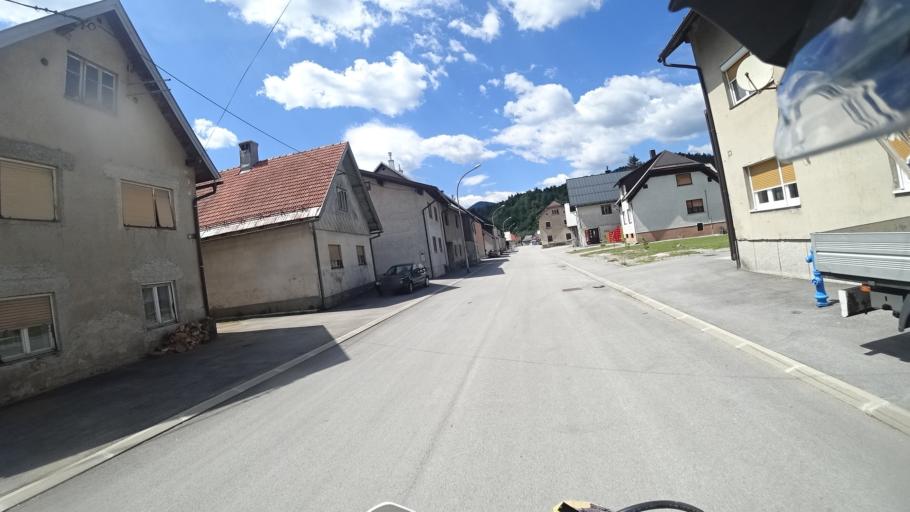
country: SI
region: Osilnica
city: Osilnica
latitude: 45.5136
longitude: 14.6421
